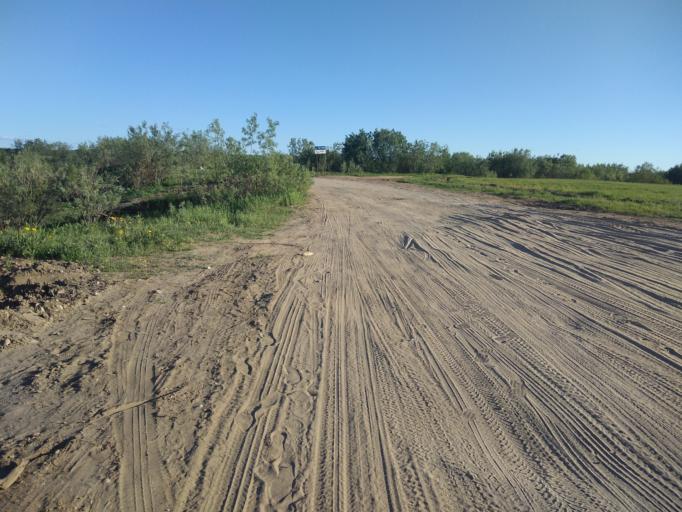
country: RU
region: Komi Republic
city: Puteyets
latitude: 65.1059
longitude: 57.1397
